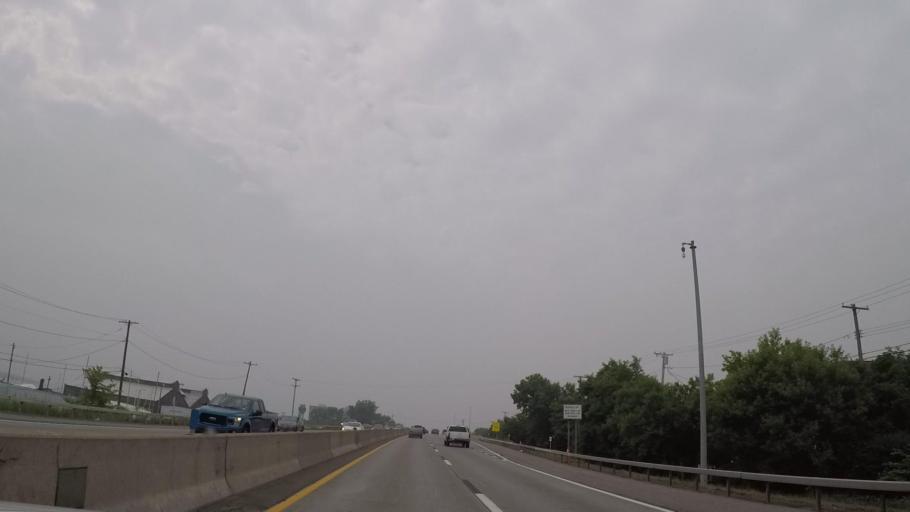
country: US
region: New York
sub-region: Erie County
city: Kenmore
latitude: 42.9352
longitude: -78.9037
